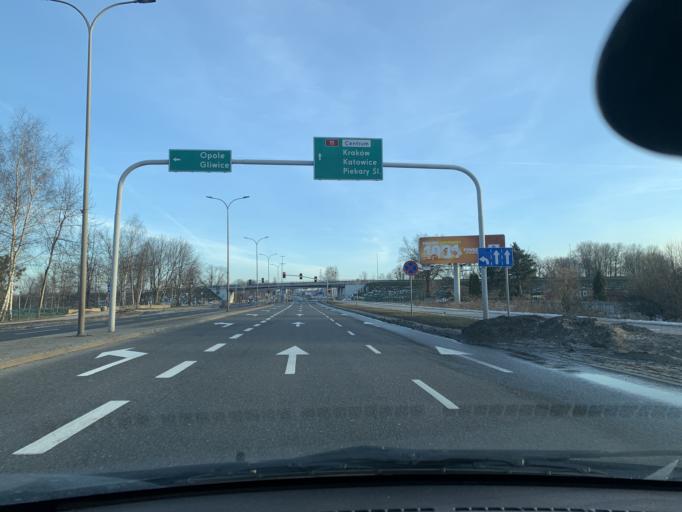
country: PL
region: Silesian Voivodeship
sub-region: Powiat tarnogorski
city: Radzionkow
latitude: 50.3701
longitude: 18.8953
